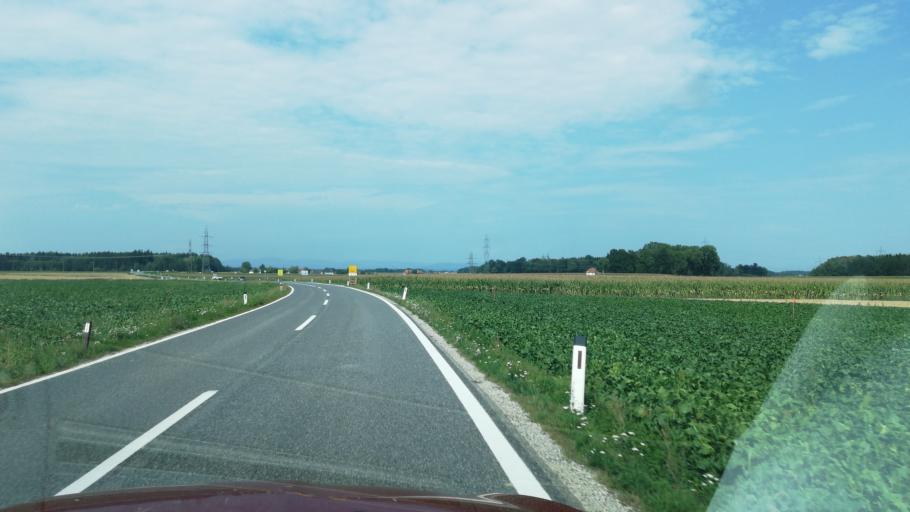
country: AT
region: Upper Austria
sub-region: Politischer Bezirk Steyr-Land
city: Sierning
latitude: 48.0845
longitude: 14.3213
